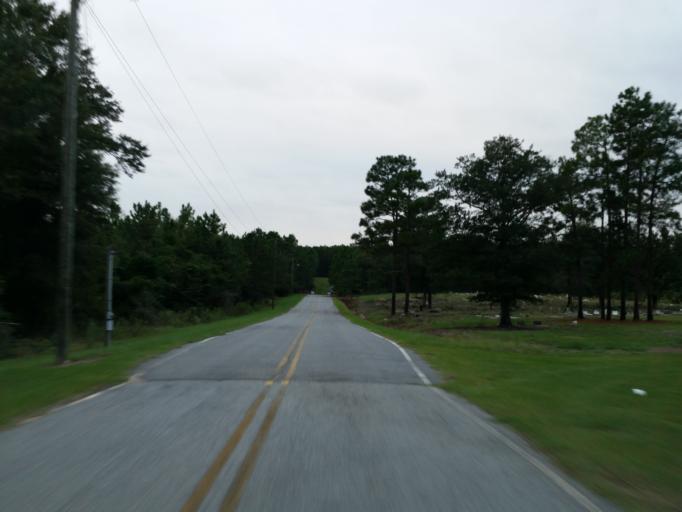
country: US
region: Georgia
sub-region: Crisp County
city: Cordele
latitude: 31.8335
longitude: -83.7461
